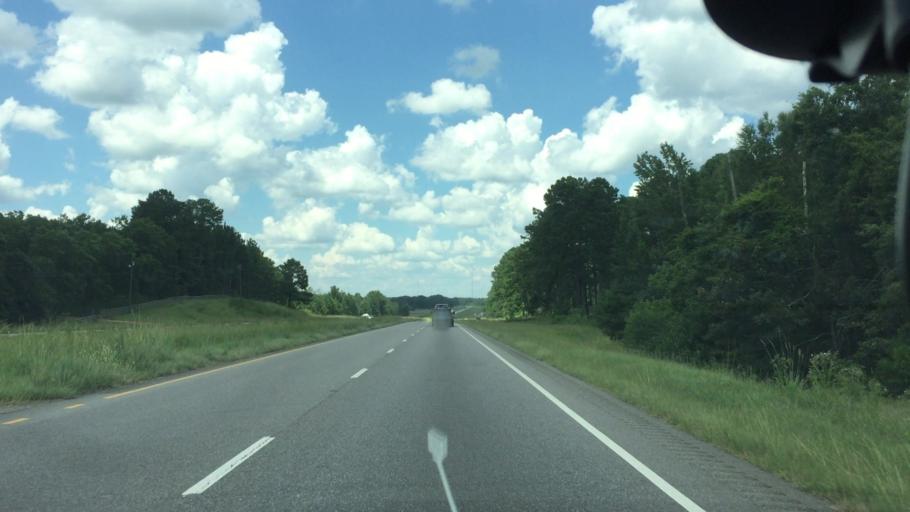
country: US
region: Alabama
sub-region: Montgomery County
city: Taylor
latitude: 32.0185
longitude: -86.0308
